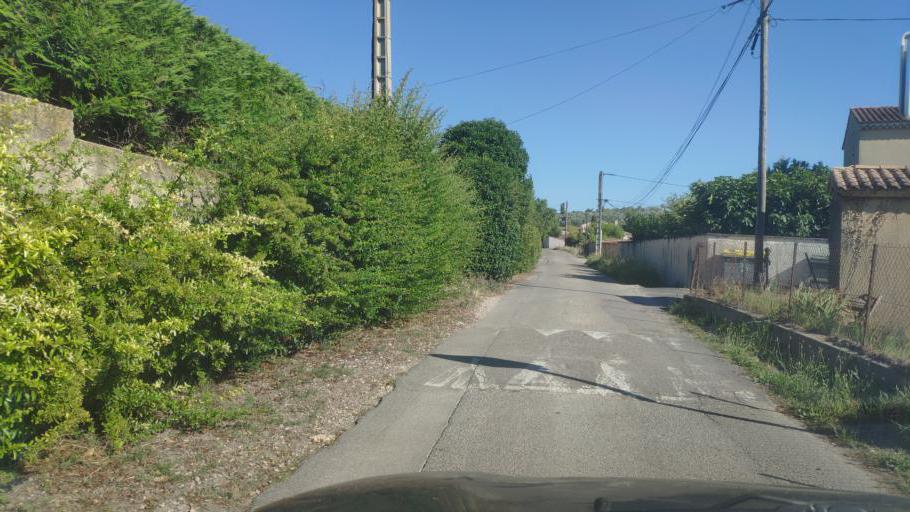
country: FR
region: Provence-Alpes-Cote d'Azur
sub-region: Departement du Vaucluse
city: Aubignan
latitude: 44.0913
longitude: 5.0359
